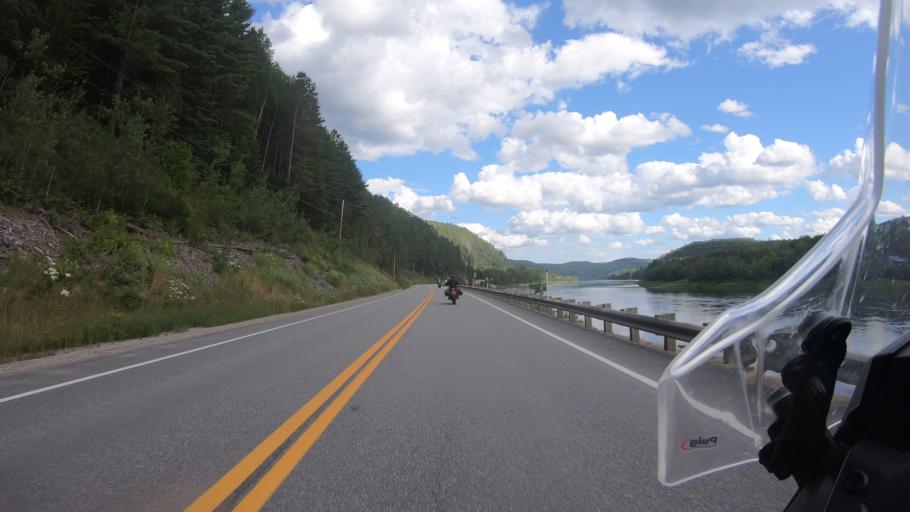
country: CA
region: Quebec
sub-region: Mauricie
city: Saint-Tite
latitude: 46.9972
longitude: -72.9212
